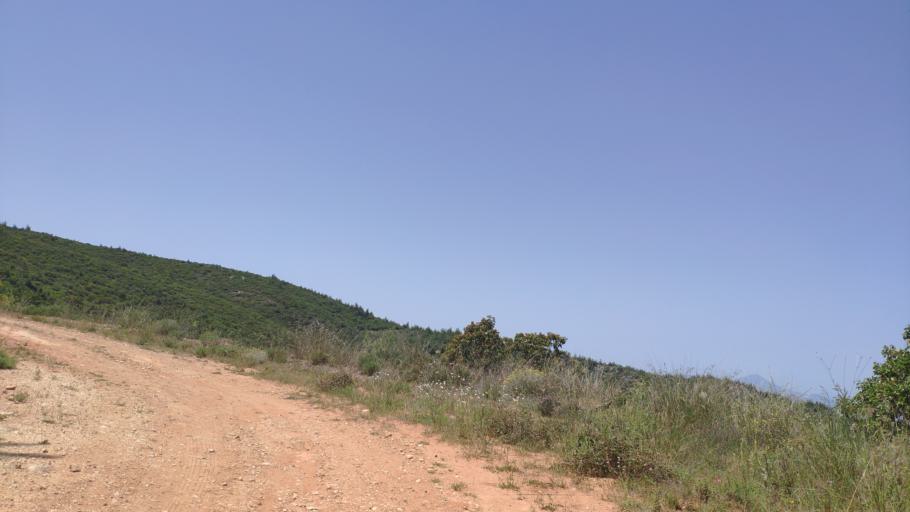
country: GR
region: Attica
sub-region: Nomarchia Anatolikis Attikis
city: Kalamos
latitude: 38.2808
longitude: 23.8490
